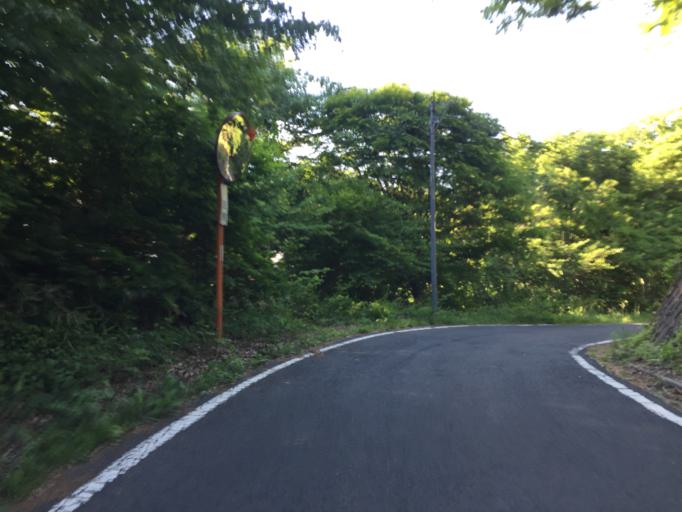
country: JP
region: Ibaraki
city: Kitaibaraki
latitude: 36.9059
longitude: 140.5873
